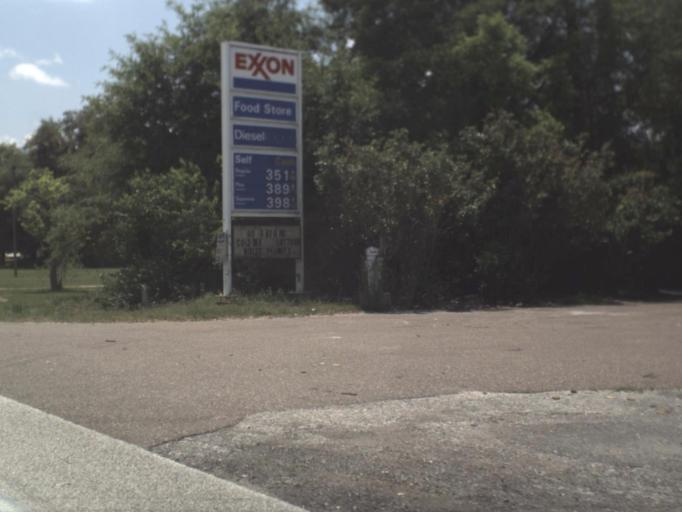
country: US
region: Florida
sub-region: Bradford County
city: Starke
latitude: 29.9041
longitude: -82.1360
